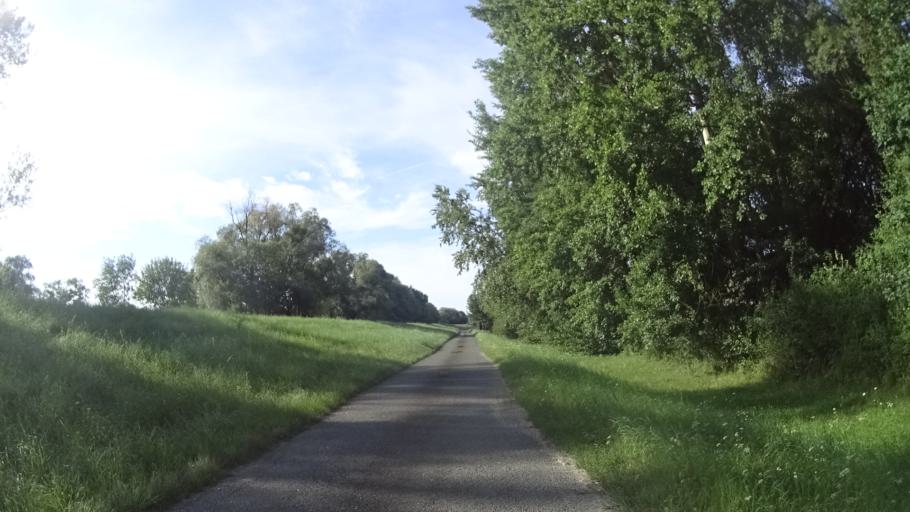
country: AT
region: Lower Austria
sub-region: Politischer Bezirk Ganserndorf
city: Drosing
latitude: 48.5538
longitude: 16.9607
